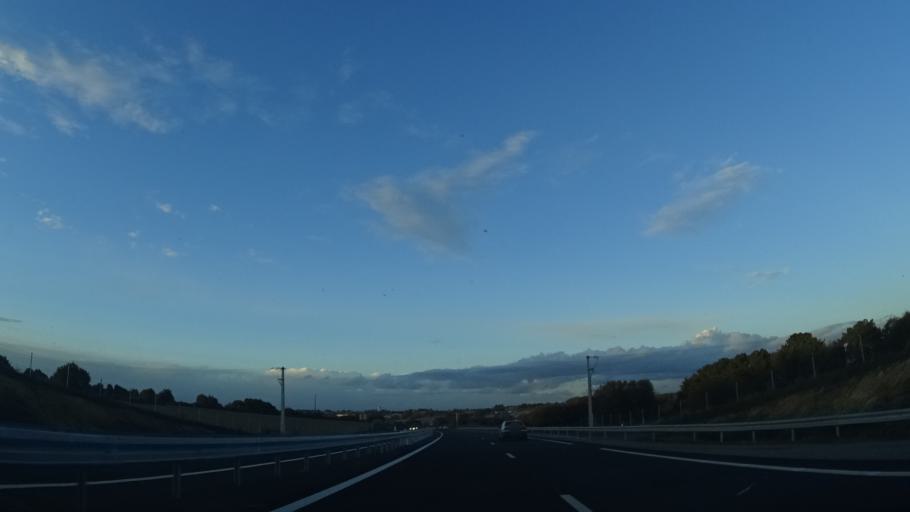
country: FR
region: Brittany
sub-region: Departement d'Ille-et-Vilaine
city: Pipriac
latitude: 47.7848
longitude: -1.9239
